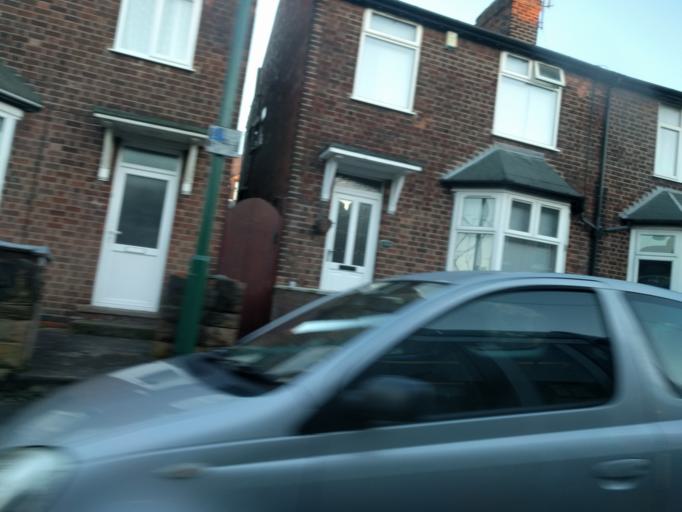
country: GB
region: England
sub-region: Nottingham
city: Nottingham
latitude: 52.9712
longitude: -1.1709
